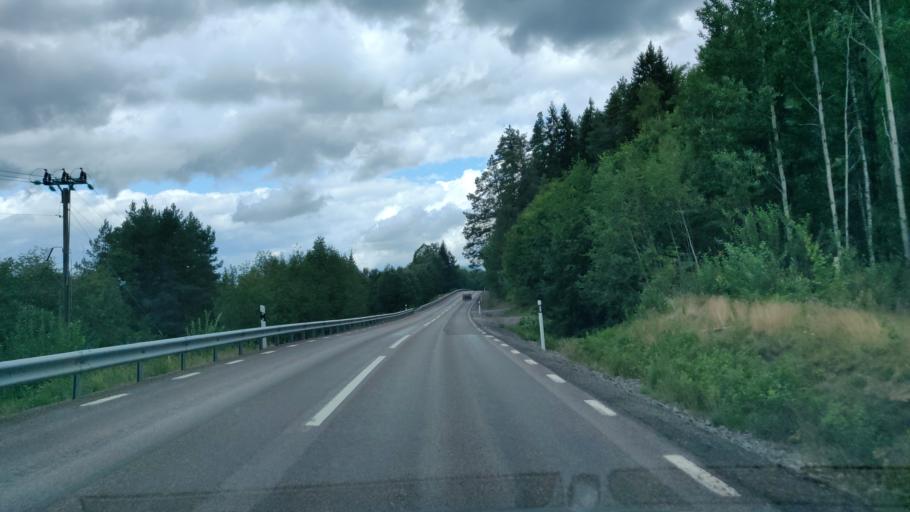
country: SE
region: Vaermland
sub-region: Torsby Kommun
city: Torsby
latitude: 60.5798
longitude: 13.0830
